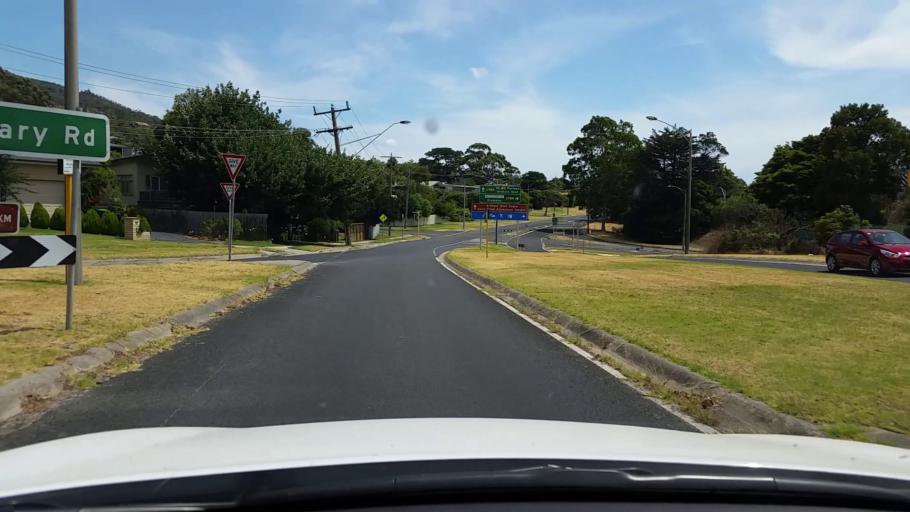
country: AU
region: Victoria
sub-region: Mornington Peninsula
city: Dromana
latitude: -38.3418
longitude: 144.9611
